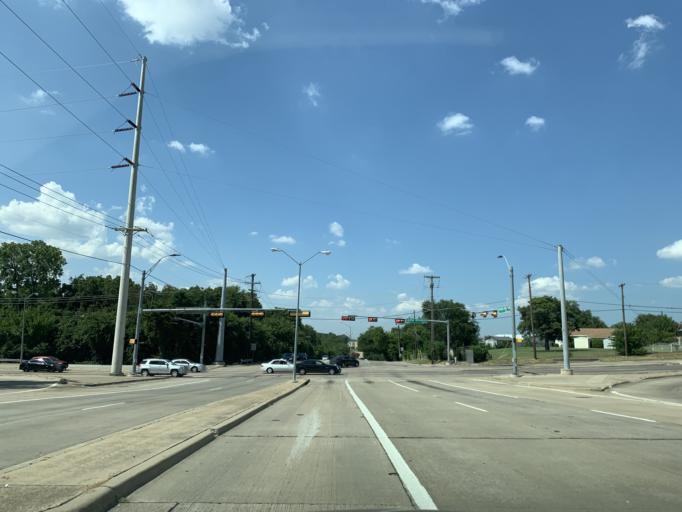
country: US
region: Texas
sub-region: Dallas County
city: Lancaster
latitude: 32.6618
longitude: -96.8057
